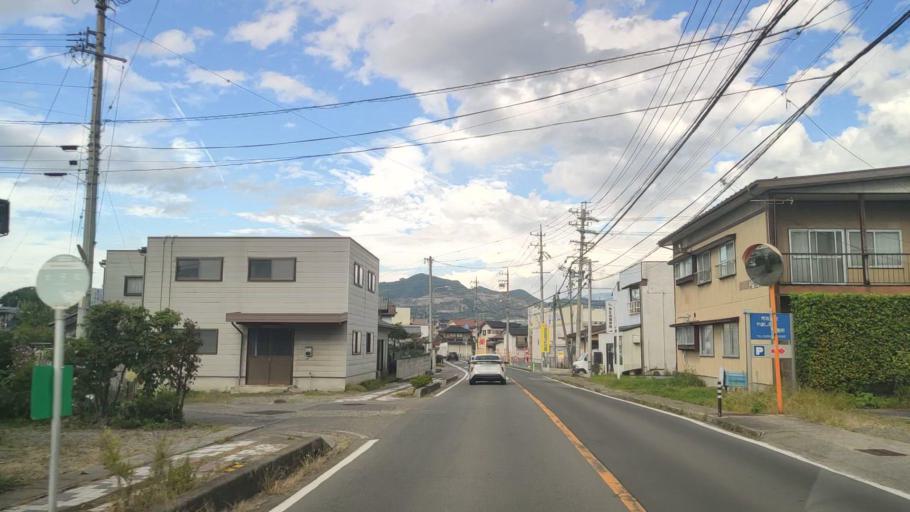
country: JP
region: Nagano
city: Suzaka
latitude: 36.6603
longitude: 138.3136
